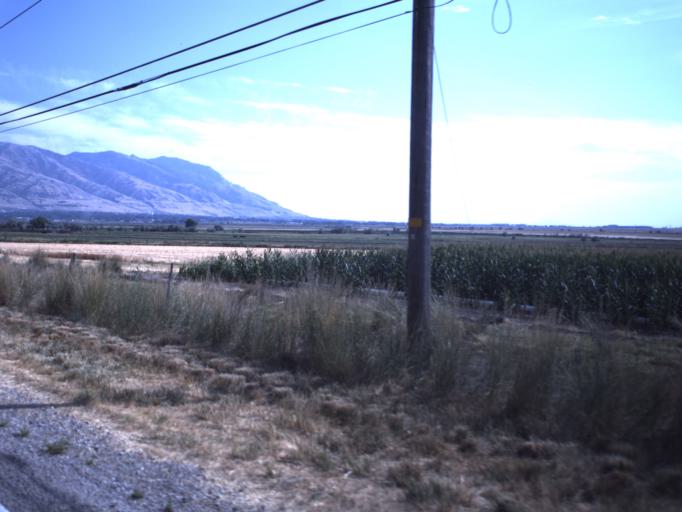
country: US
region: Utah
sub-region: Box Elder County
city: Honeyville
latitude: 41.5862
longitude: -112.0405
